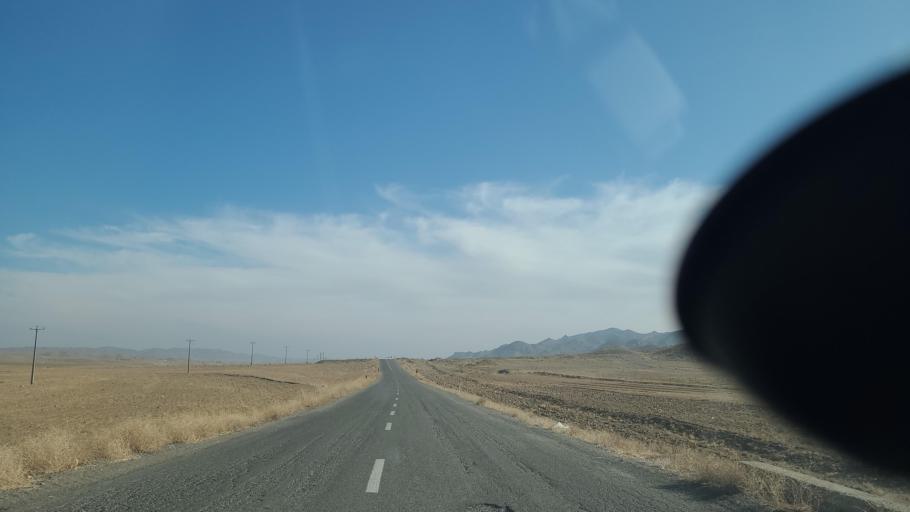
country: IR
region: Razavi Khorasan
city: Fariman
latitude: 35.5873
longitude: 59.6420
